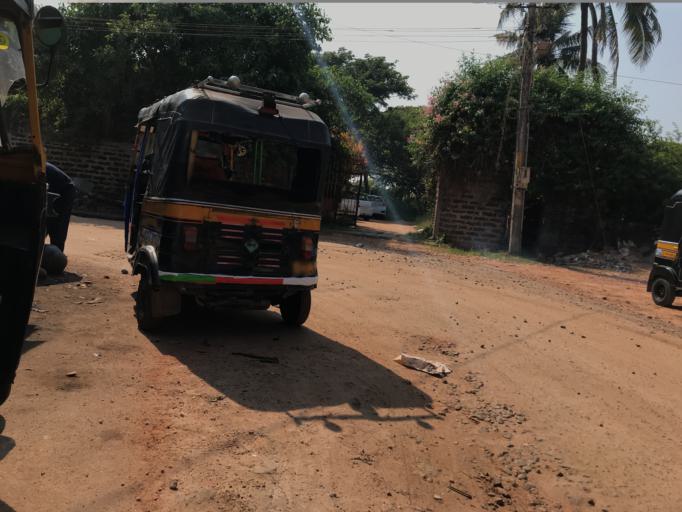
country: IN
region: Karnataka
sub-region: Dakshina Kannada
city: Mangalore
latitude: 12.8701
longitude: 74.8312
